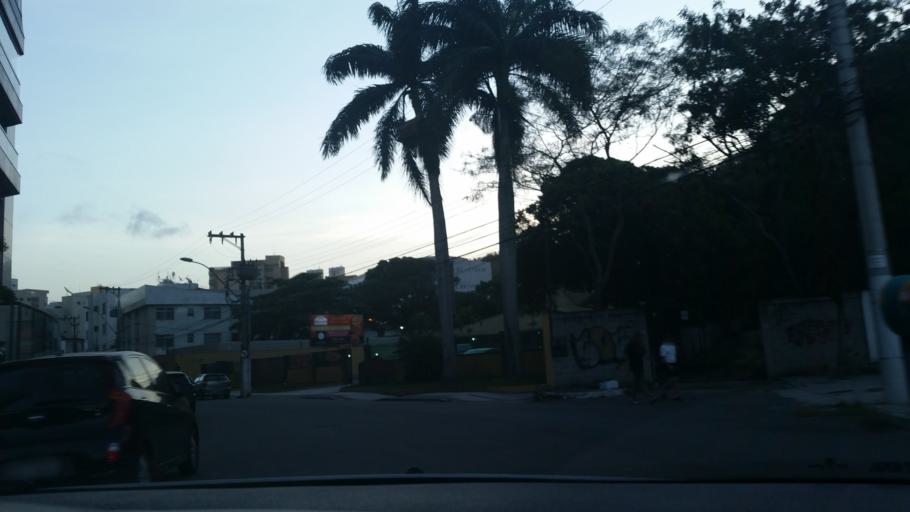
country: BR
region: Espirito Santo
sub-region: Vila Velha
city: Vila Velha
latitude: -20.3283
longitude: -40.2739
